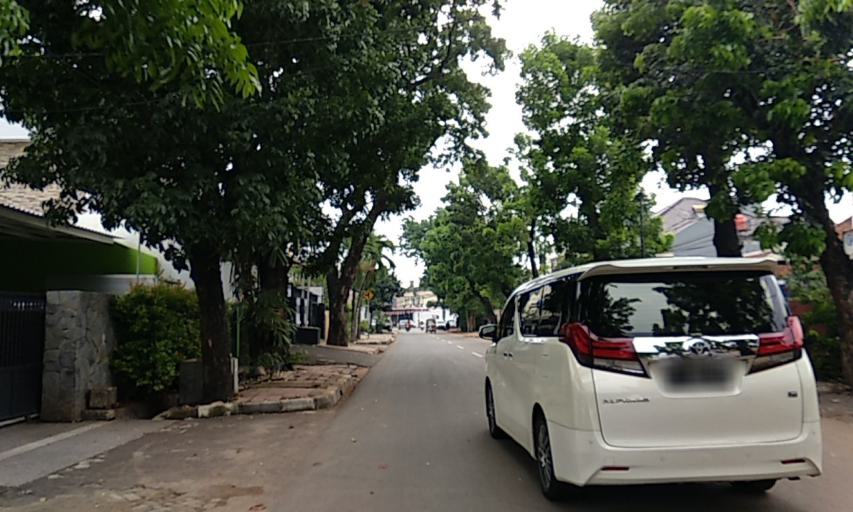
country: ID
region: Jakarta Raya
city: Jakarta
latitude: -6.2405
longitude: 106.8545
